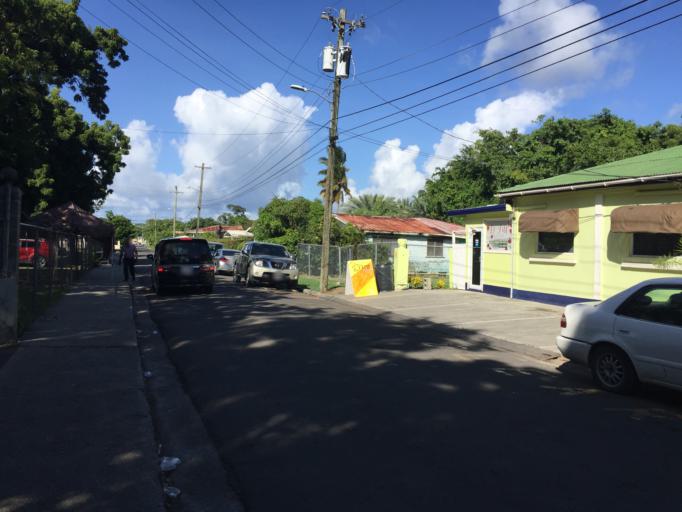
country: AG
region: Saint John
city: Saint John's
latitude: 17.1262
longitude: -61.8418
